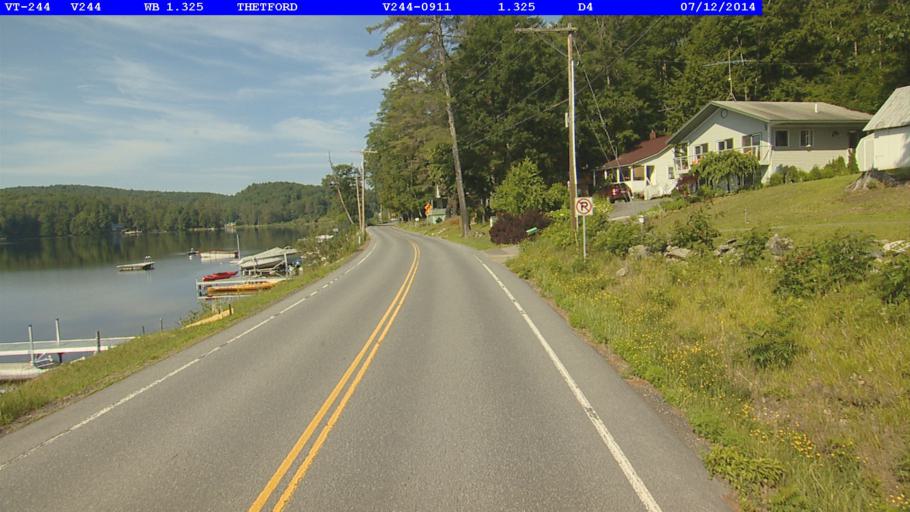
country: US
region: New Hampshire
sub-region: Grafton County
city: Orford
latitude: 43.8878
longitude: -72.2354
